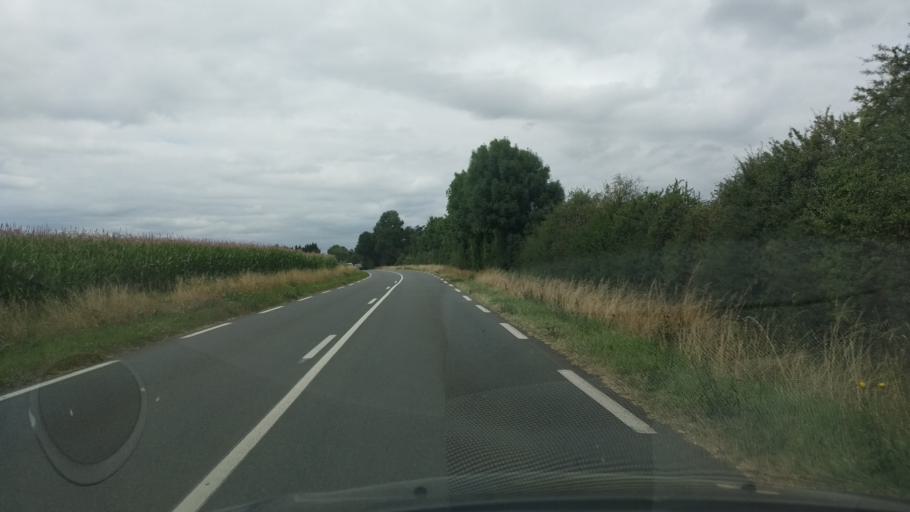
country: FR
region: Poitou-Charentes
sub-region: Departement de la Vienne
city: La Villedieu-du-Clain
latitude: 46.4457
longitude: 0.3699
